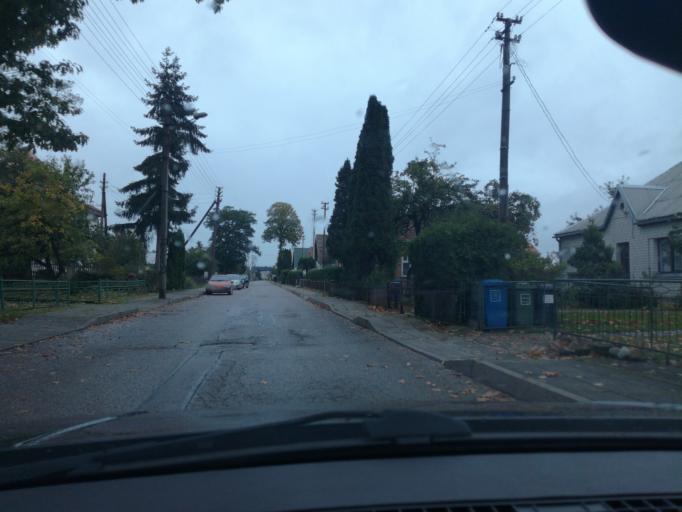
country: LT
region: Alytaus apskritis
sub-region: Alytus
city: Alytus
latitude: 54.3978
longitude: 24.0581
